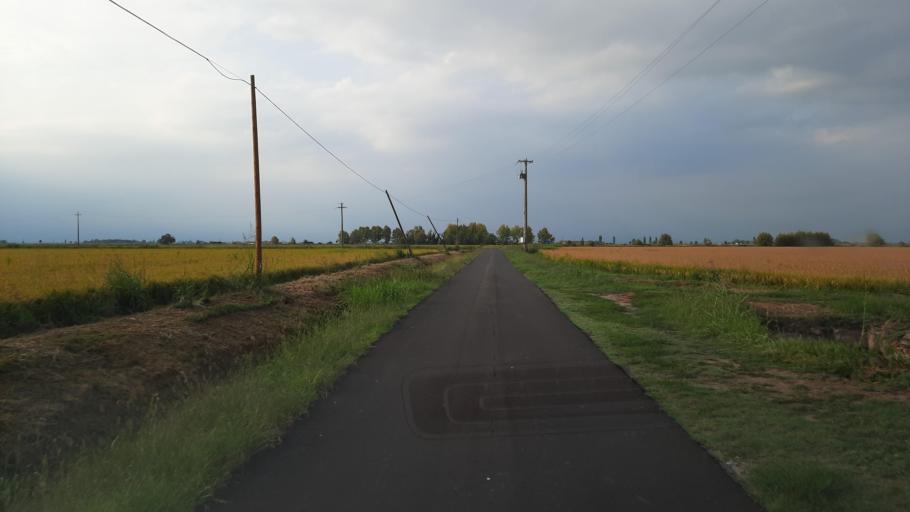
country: IT
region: Piedmont
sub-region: Provincia di Vercelli
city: Sali Vercellese
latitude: 45.3202
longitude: 8.3478
